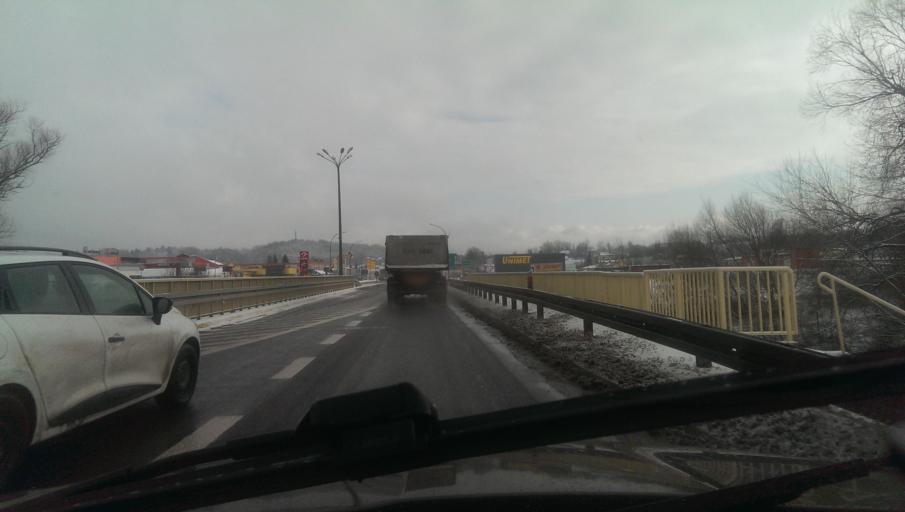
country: PL
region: Subcarpathian Voivodeship
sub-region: Powiat sanocki
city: Sanok
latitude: 49.5694
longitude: 22.1516
